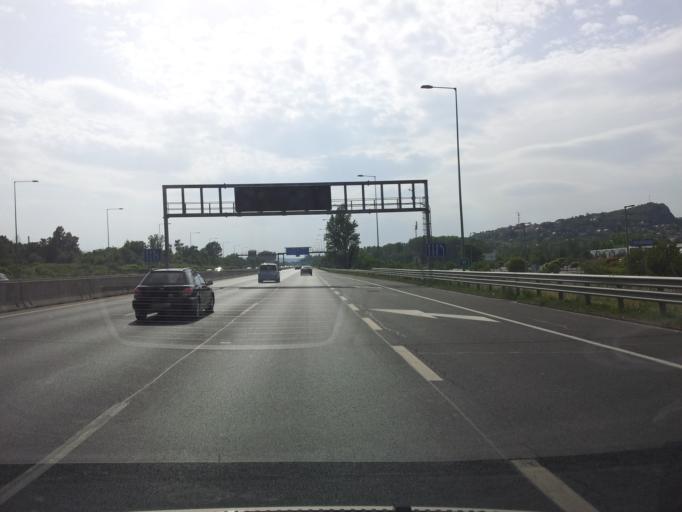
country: HU
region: Pest
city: Budaors
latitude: 47.4522
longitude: 18.9398
